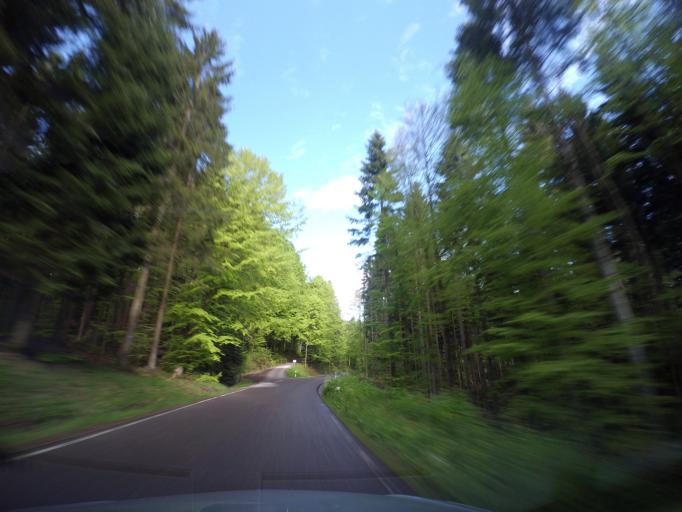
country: DE
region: Baden-Wuerttemberg
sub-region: Regierungsbezirk Stuttgart
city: Gschwend
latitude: 48.9542
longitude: 9.7267
